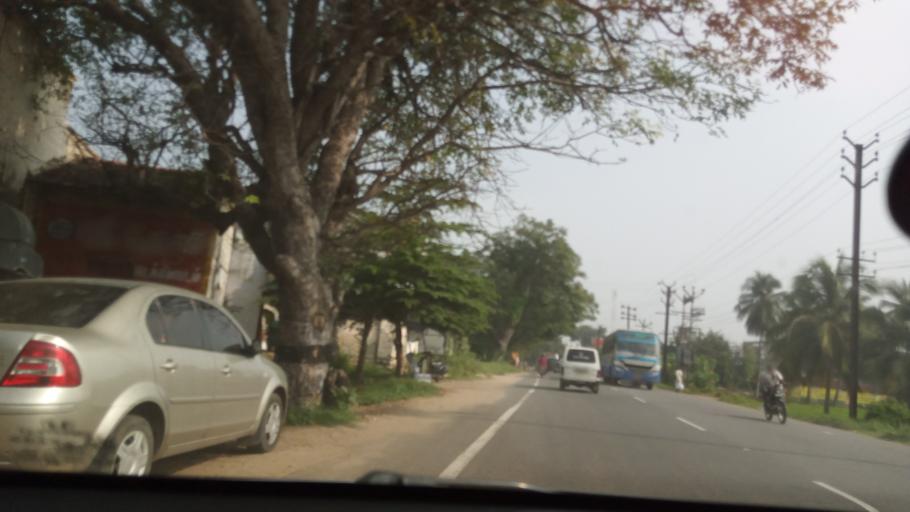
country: IN
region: Tamil Nadu
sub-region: Erode
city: Punjai Puliyampatti
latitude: 11.3460
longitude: 77.1636
